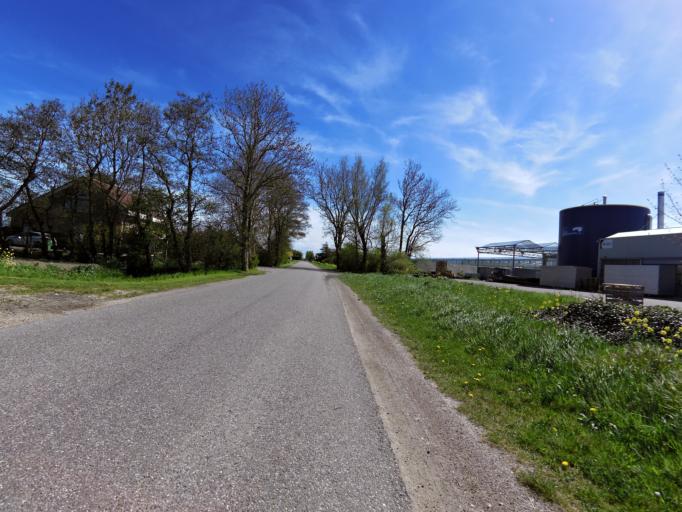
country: NL
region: South Holland
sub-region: Gemeente Brielle
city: Brielle
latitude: 51.8981
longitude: 4.1402
